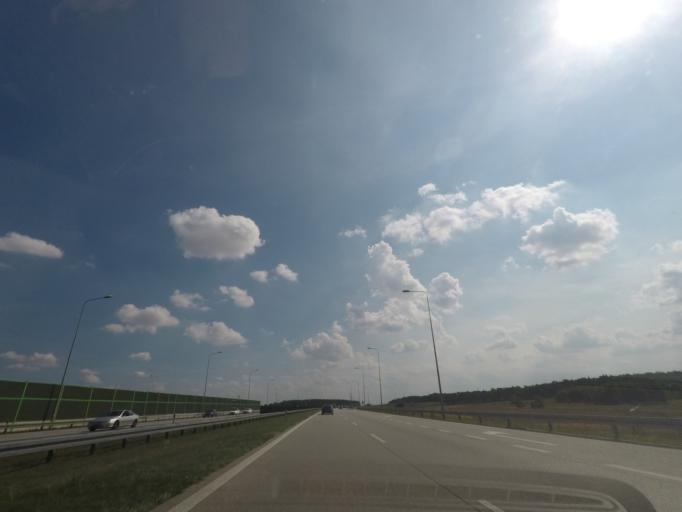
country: PL
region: Lodz Voivodeship
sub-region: Powiat piotrkowski
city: Czarnocin
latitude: 51.5540
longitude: 19.6044
